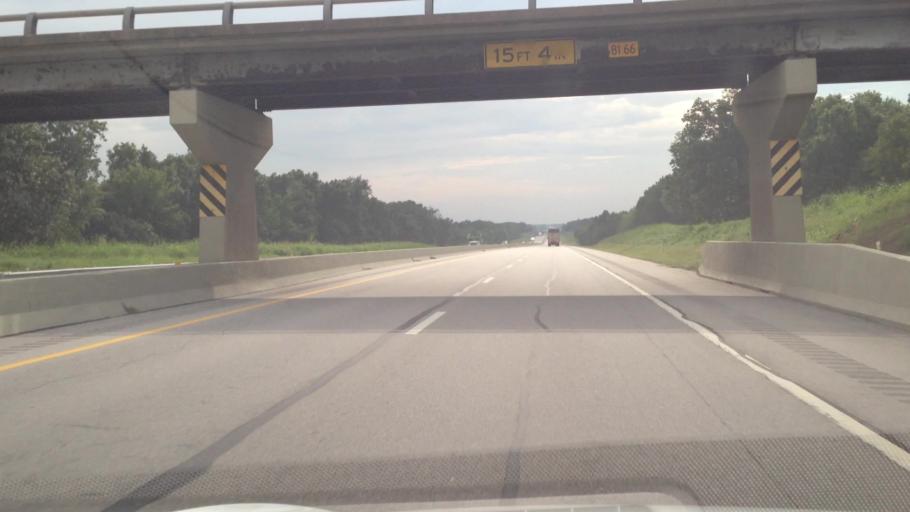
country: US
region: Kansas
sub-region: Cherokee County
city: Baxter Springs
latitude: 36.9344
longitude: -94.7121
